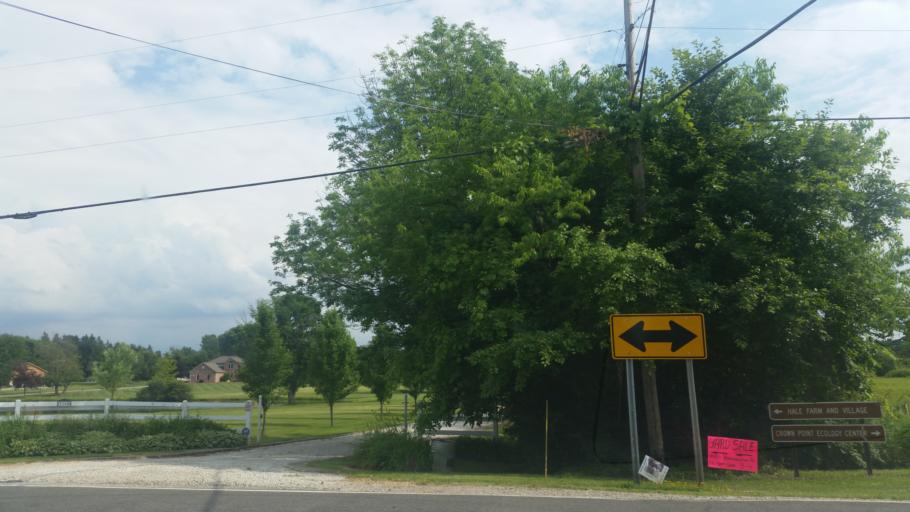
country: US
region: Ohio
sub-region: Summit County
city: Montrose-Ghent
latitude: 41.1891
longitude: -81.6163
